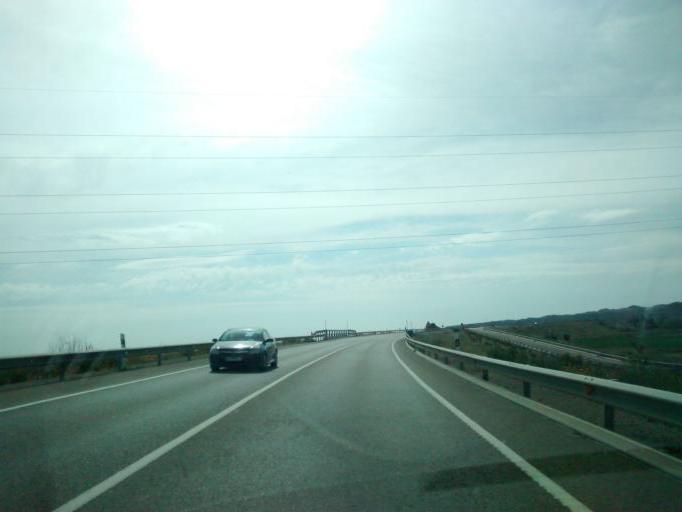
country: ES
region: Aragon
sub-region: Provincia de Zaragoza
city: El Burgo de Ebro
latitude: 41.5773
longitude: -0.7567
